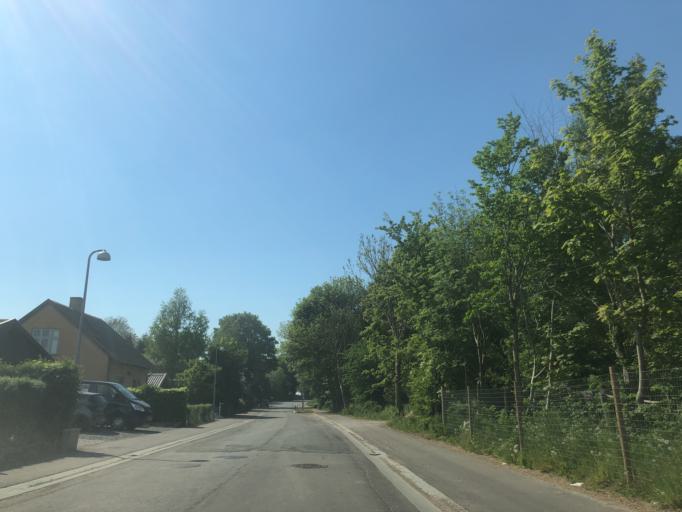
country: DK
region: Capital Region
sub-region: Hoje-Taastrup Kommune
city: Taastrup
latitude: 55.6263
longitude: 12.2503
